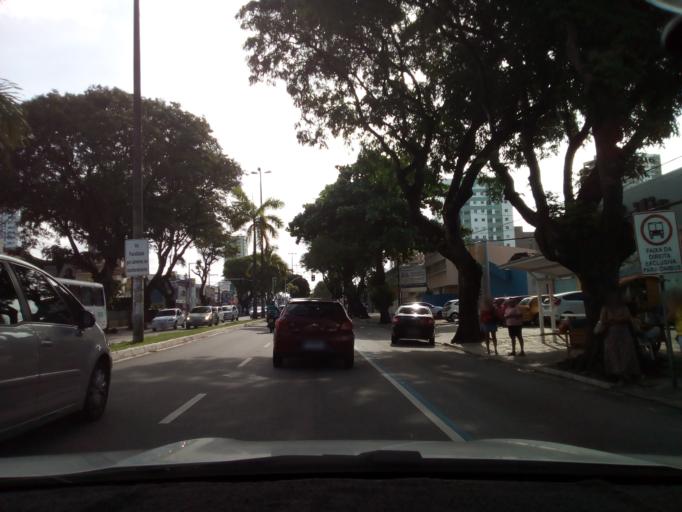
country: BR
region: Paraiba
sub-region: Joao Pessoa
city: Joao Pessoa
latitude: -7.1195
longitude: -34.8380
